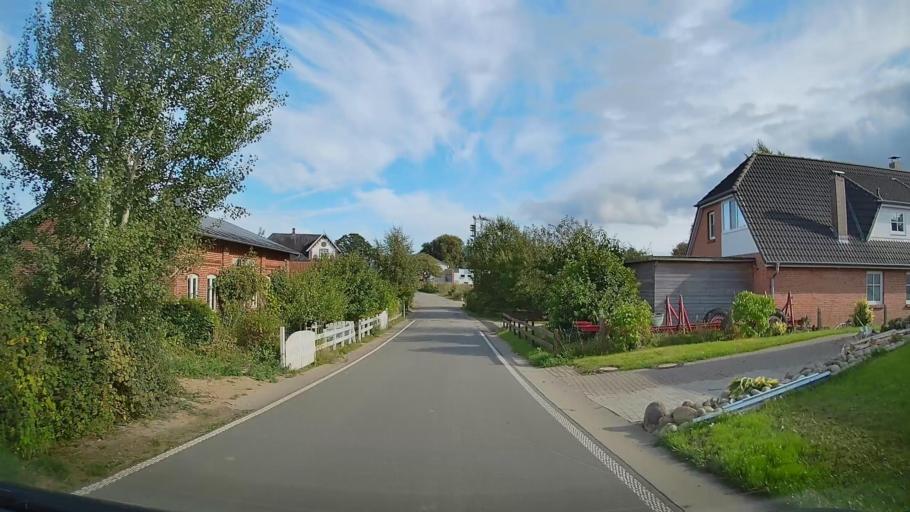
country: DE
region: Schleswig-Holstein
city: Steinberg
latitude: 54.8004
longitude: 9.7537
